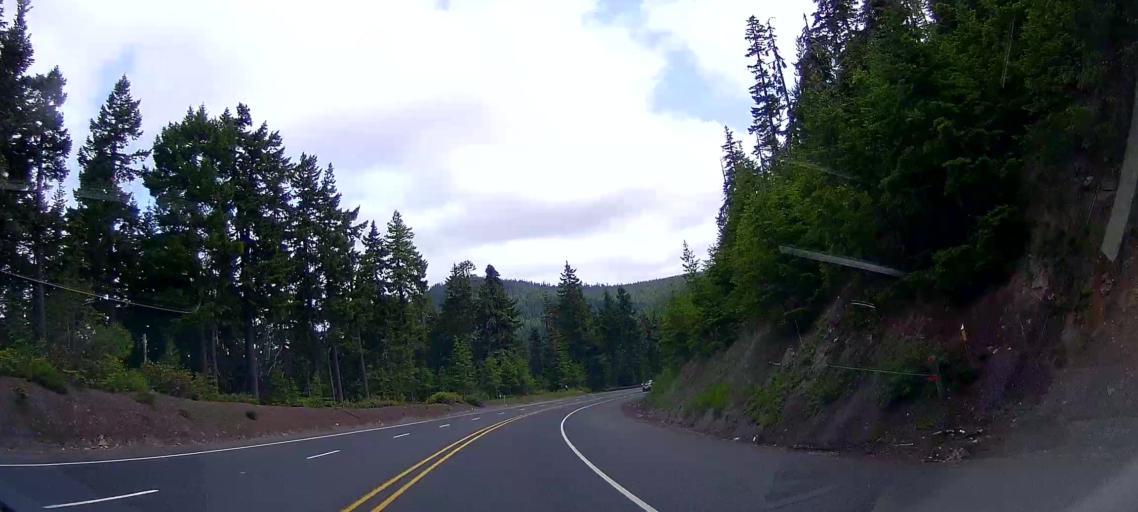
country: US
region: Oregon
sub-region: Clackamas County
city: Mount Hood Village
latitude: 45.2323
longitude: -121.7021
